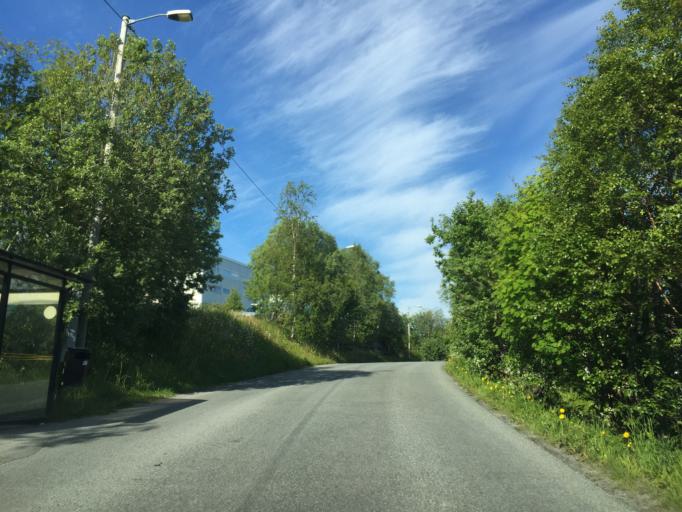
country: NO
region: Nordland
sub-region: Bodo
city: Lopsmarka
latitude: 67.2810
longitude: 14.5321
